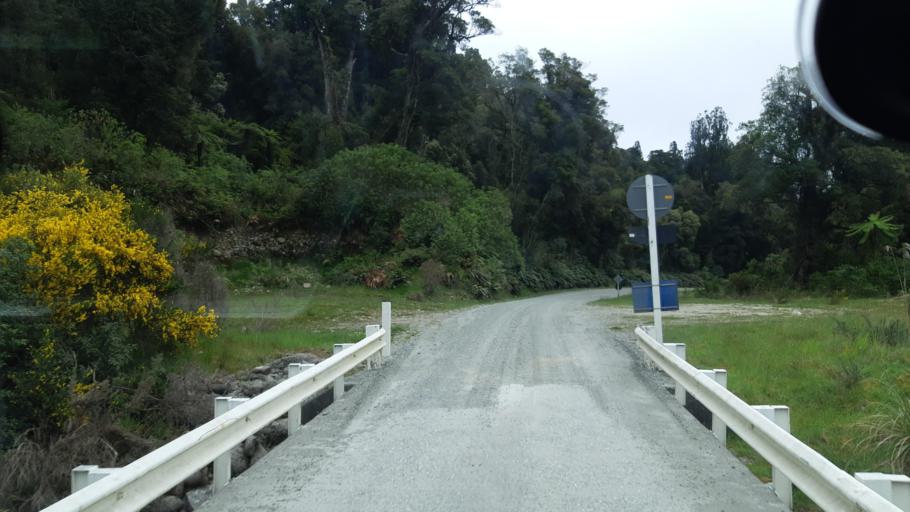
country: NZ
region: West Coast
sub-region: Grey District
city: Greymouth
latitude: -42.6496
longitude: 171.3067
